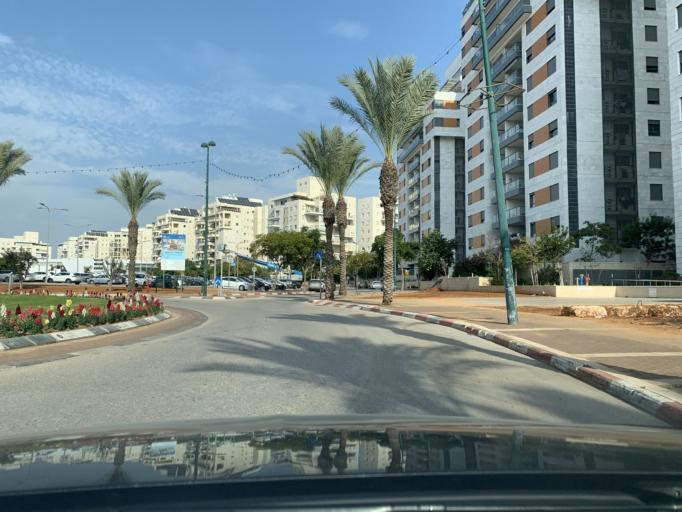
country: IL
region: Central District
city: Ganne Tiqwa
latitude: 32.0543
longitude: 34.8577
